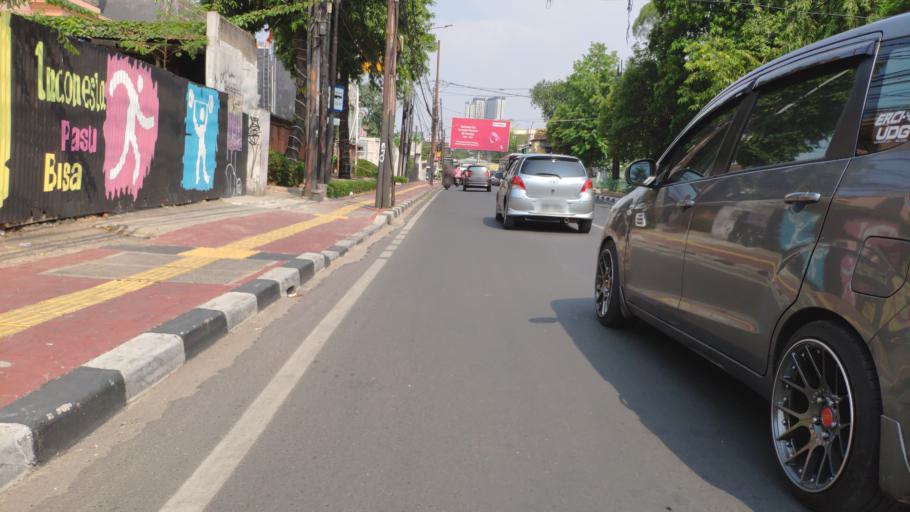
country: ID
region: Jakarta Raya
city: Jakarta
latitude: -6.2740
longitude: 106.8201
